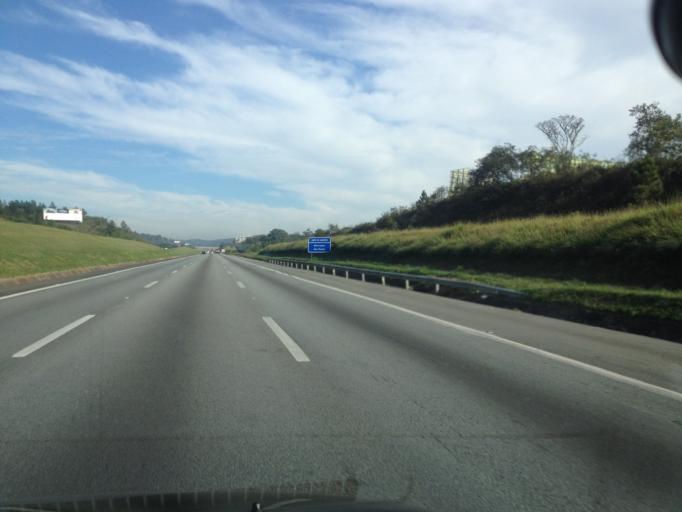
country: BR
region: Sao Paulo
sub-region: Sao Roque
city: Sao Roque
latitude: -23.4204
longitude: -47.1856
